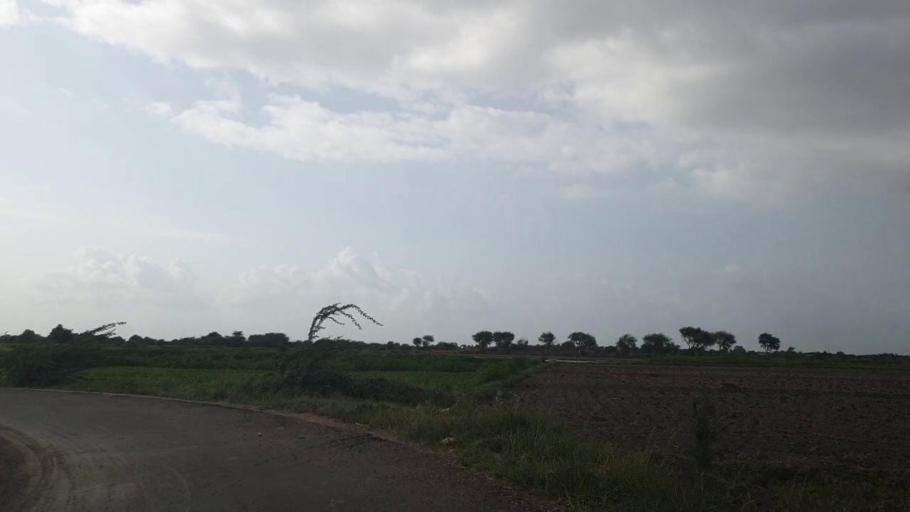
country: PK
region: Sindh
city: Kadhan
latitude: 24.6016
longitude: 69.0563
